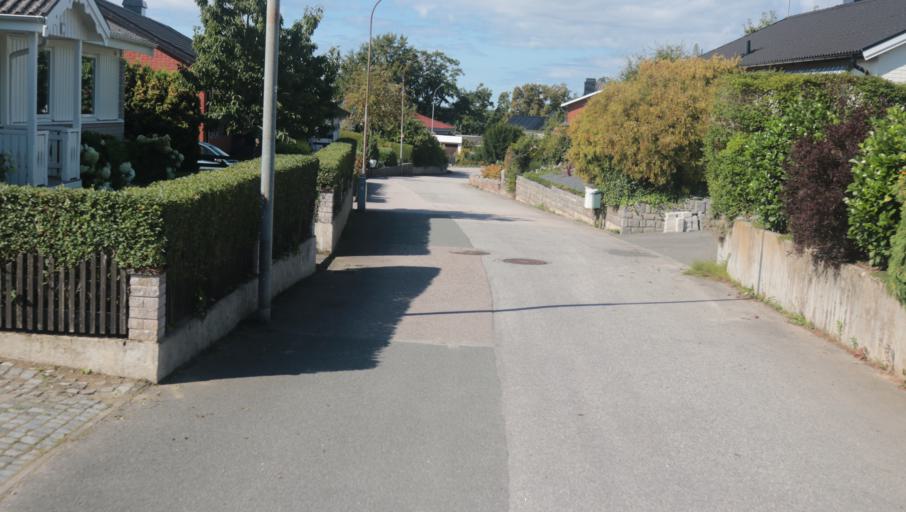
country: SE
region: Blekinge
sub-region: Karlshamns Kommun
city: Karlshamn
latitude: 56.1838
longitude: 14.8655
